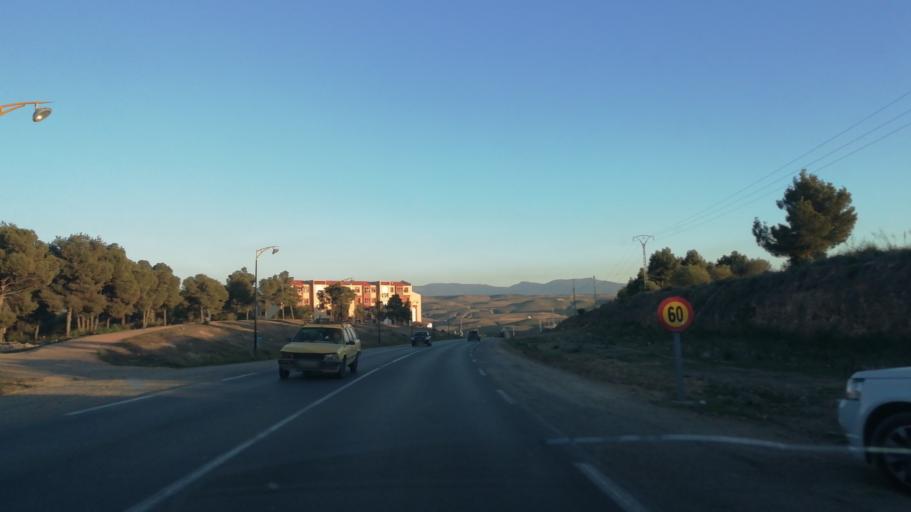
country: DZ
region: Tlemcen
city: Nedroma
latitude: 34.8905
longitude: -1.6549
